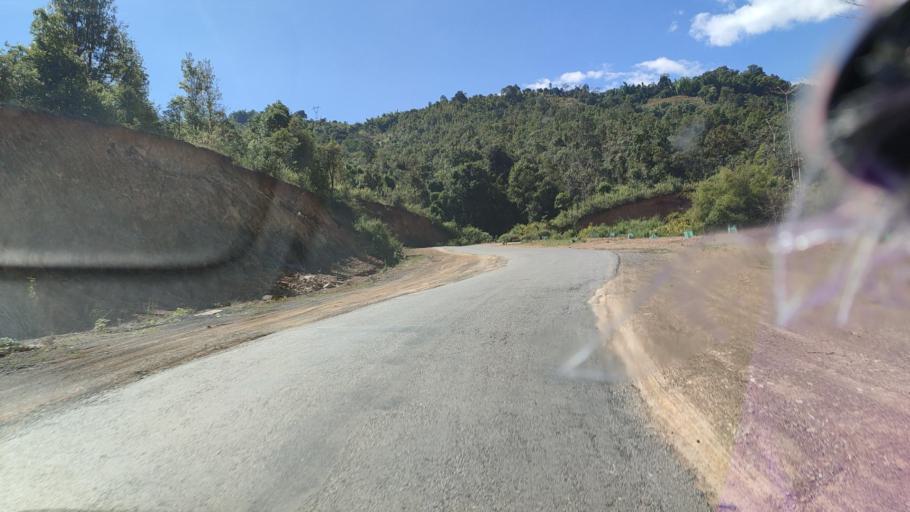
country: MM
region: Shan
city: Taunggyi
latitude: 20.8280
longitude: 97.3618
